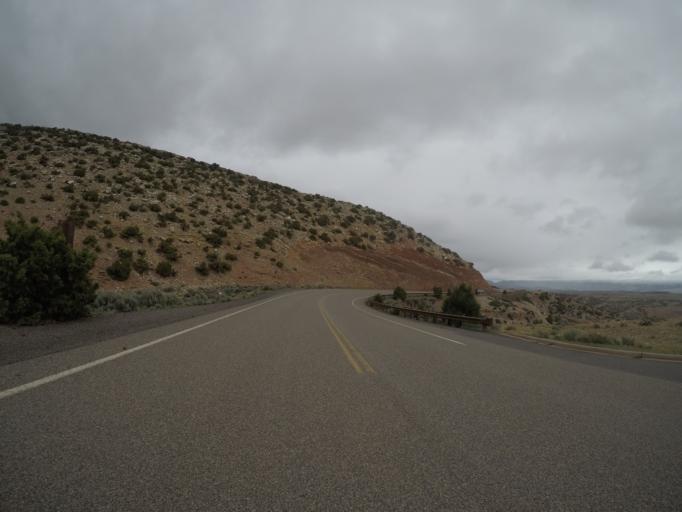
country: US
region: Wyoming
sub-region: Big Horn County
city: Lovell
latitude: 45.0413
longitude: -108.2531
